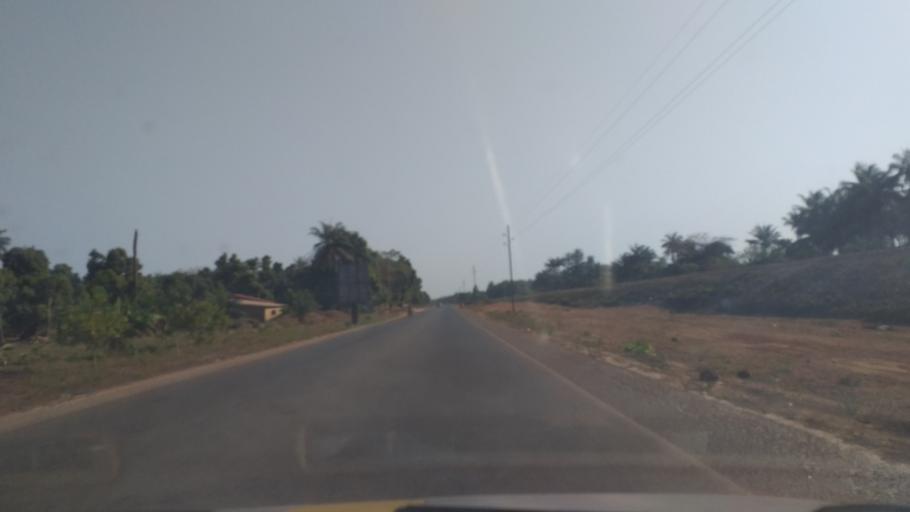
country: GN
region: Boke
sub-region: Boke Prefecture
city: Kamsar
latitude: 10.7506
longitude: -14.5081
